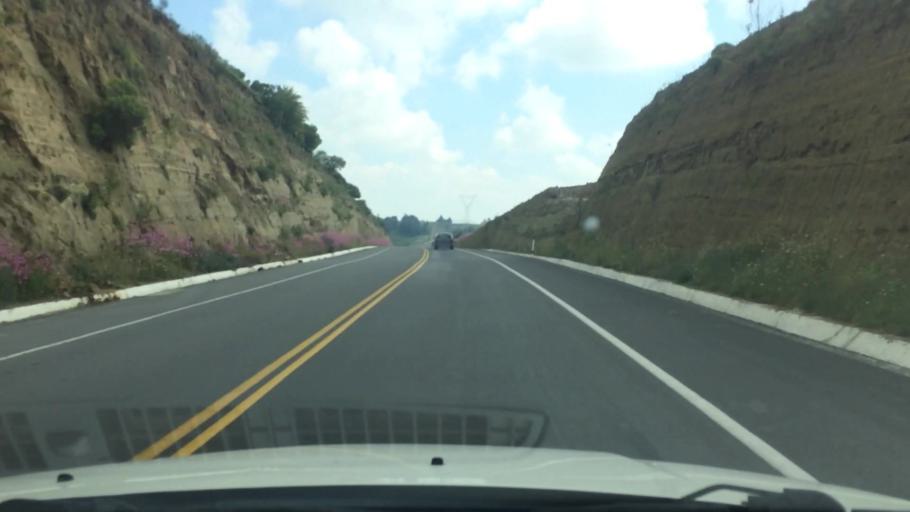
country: MX
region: Mexico
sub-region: Villa Victoria
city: Colonia Doctor Gustavo Baz
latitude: 19.3642
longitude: -99.9450
